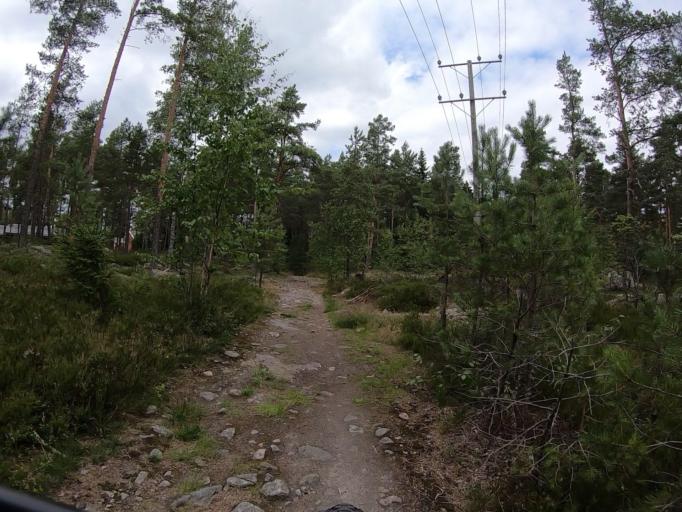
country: FI
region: Varsinais-Suomi
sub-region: Vakka-Suomi
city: Uusikaupunki
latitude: 60.8211
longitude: 21.4139
